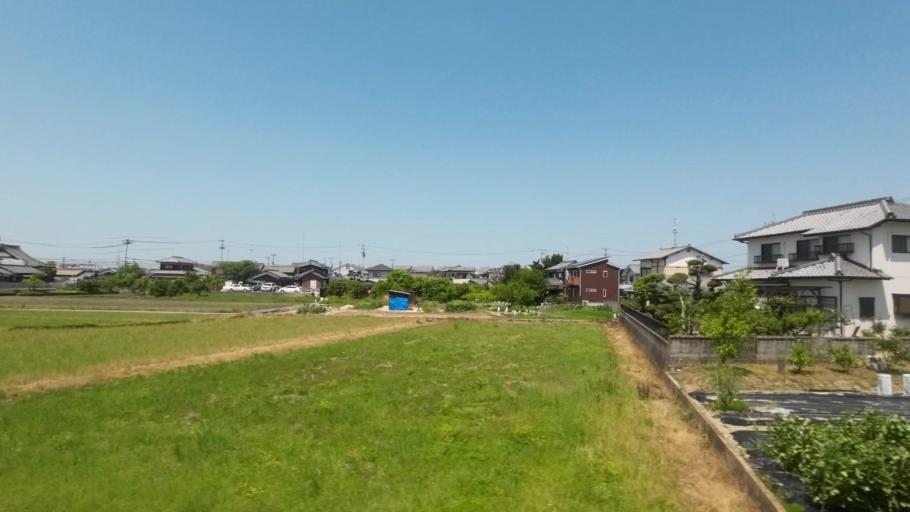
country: JP
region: Ehime
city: Hojo
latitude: 33.9411
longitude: 132.7697
